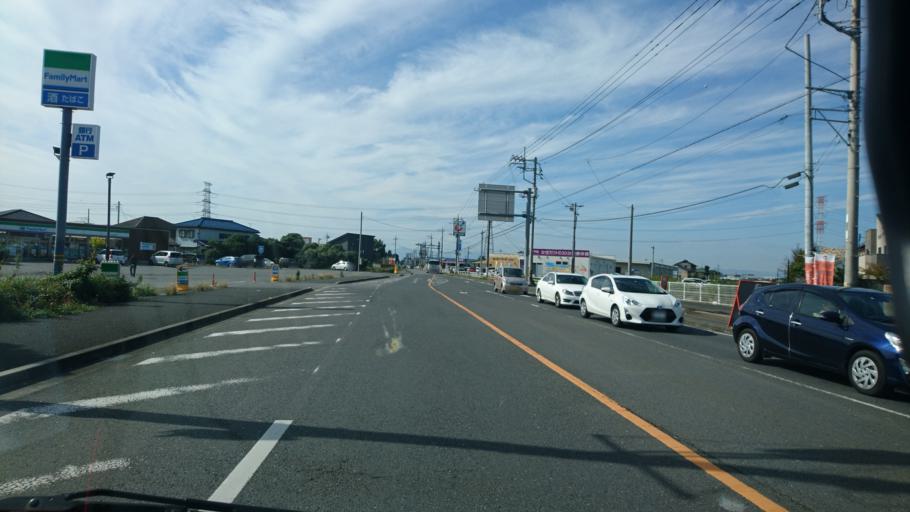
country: JP
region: Gunma
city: Kiryu
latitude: 36.3662
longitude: 139.2797
